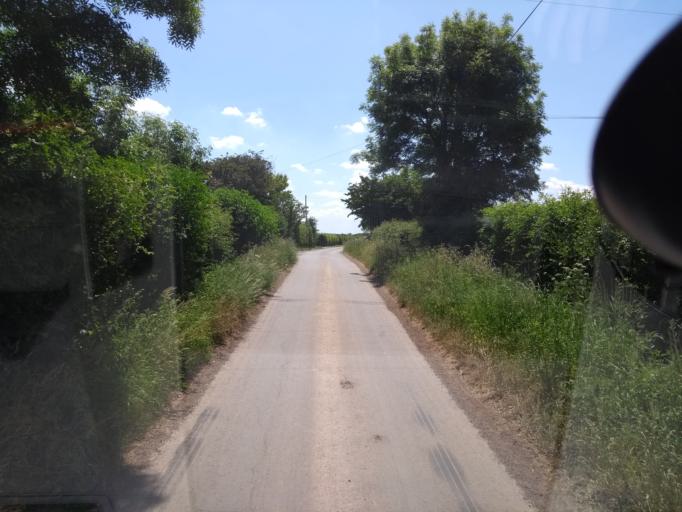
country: GB
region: England
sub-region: Somerset
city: North Petherton
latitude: 51.0567
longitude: -2.9998
